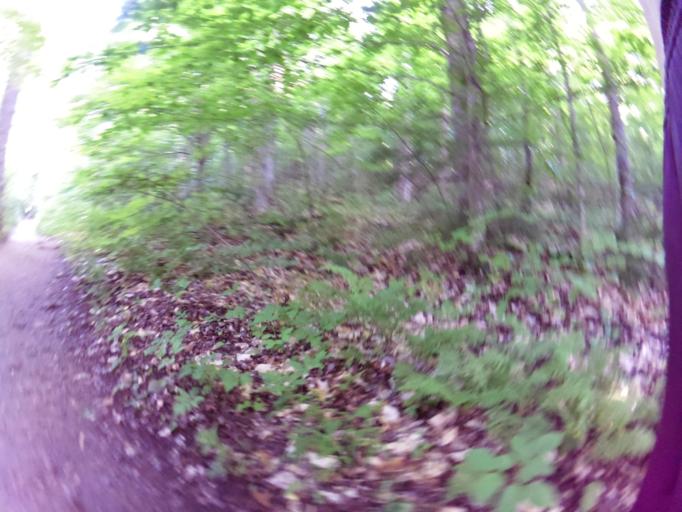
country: CA
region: Quebec
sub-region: Outaouais
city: Wakefield
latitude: 45.5885
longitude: -75.9803
